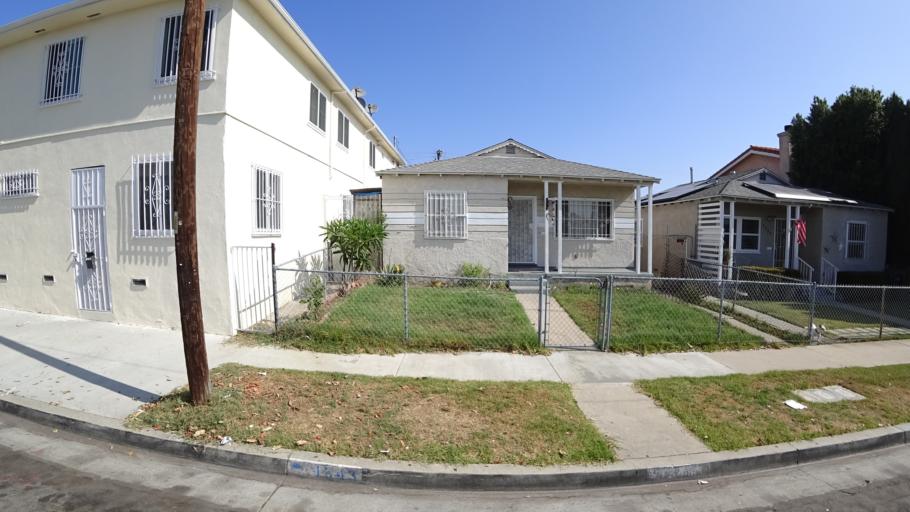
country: US
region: California
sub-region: Los Angeles County
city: Westmont
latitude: 33.9450
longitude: -118.2997
